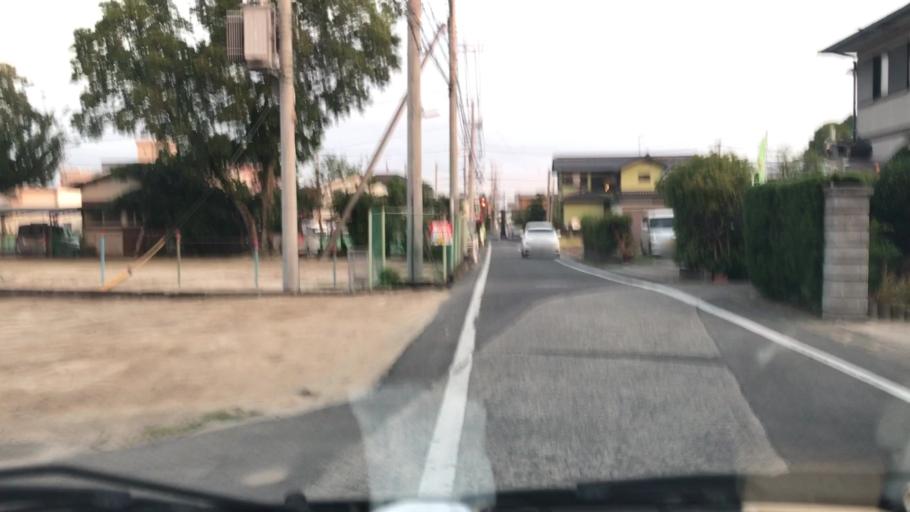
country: JP
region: Saga Prefecture
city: Saga-shi
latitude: 33.2445
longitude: 130.2577
